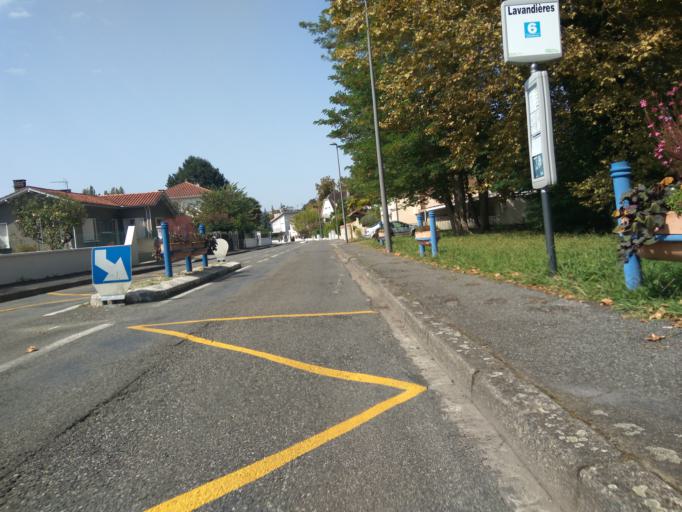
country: FR
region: Aquitaine
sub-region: Departement des Pyrenees-Atlantiques
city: Bizanos
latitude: 43.2930
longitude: -0.3488
